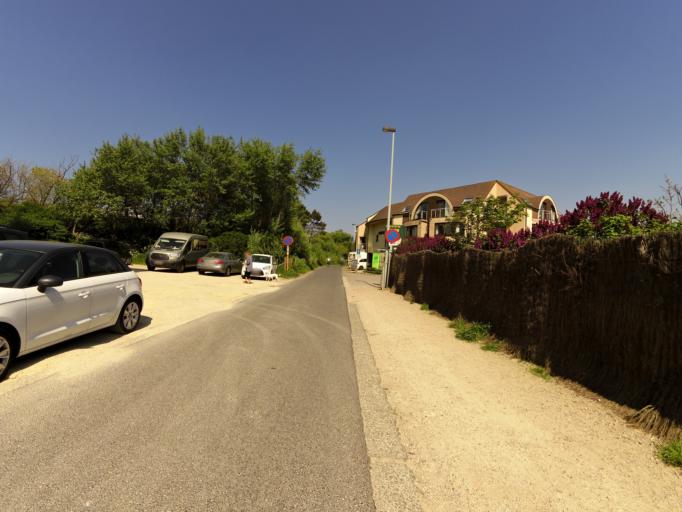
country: BE
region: Flanders
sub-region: Provincie West-Vlaanderen
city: Middelkerke
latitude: 51.1885
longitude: 2.8218
